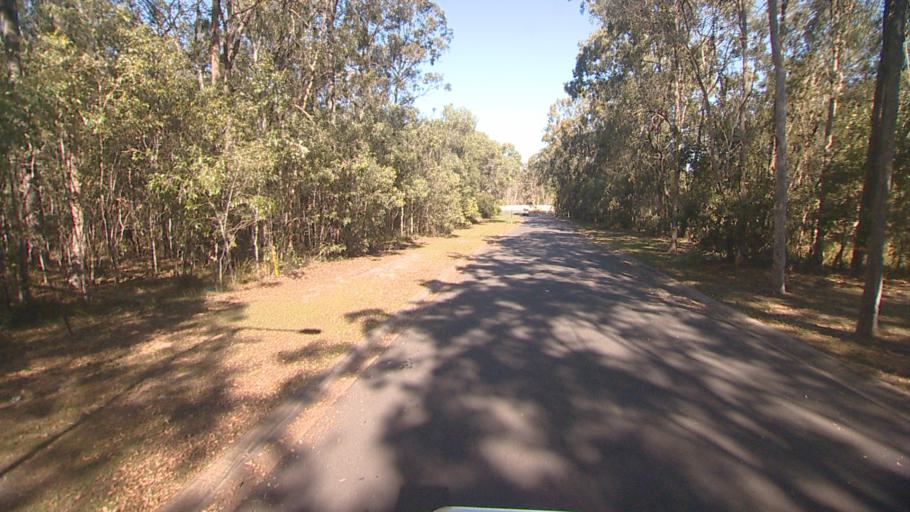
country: AU
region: Queensland
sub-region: Logan
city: Park Ridge South
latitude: -27.7161
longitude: 153.0458
